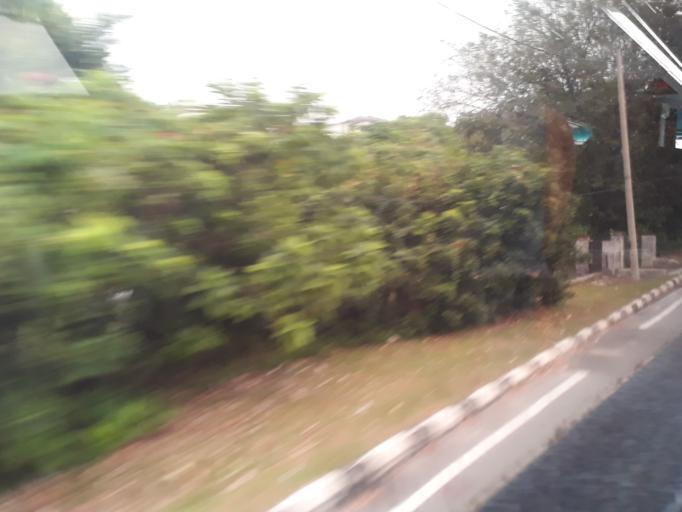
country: MY
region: Perak
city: Ipoh
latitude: 4.6013
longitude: 101.0980
